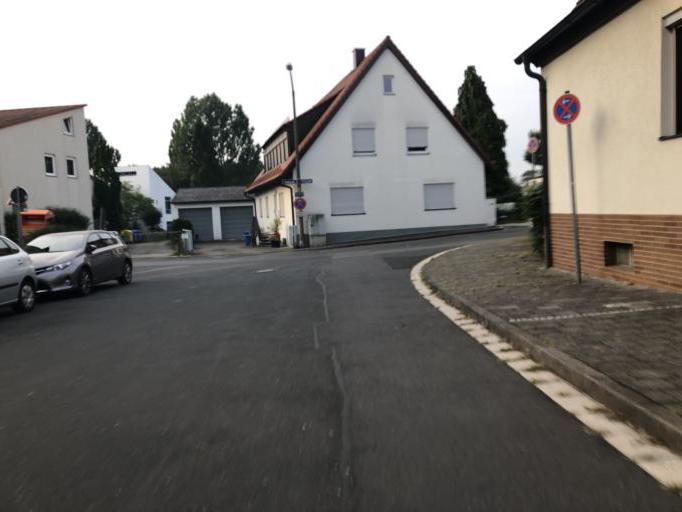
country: DE
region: Bavaria
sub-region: Regierungsbezirk Mittelfranken
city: Erlangen
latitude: 49.5892
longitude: 10.9628
